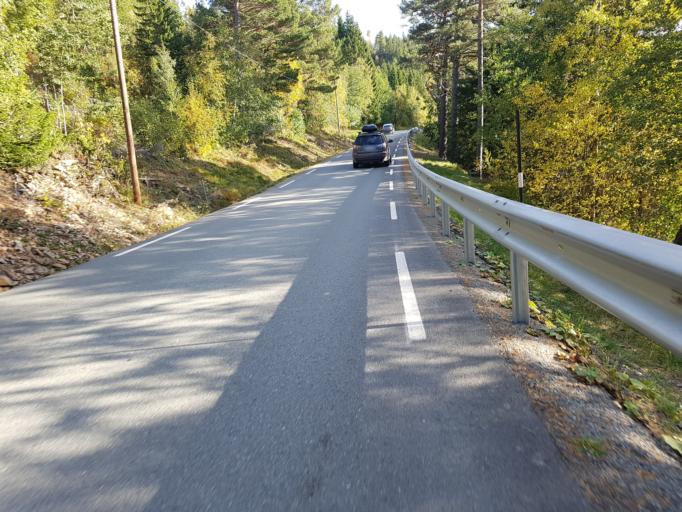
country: NO
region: Sor-Trondelag
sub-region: Malvik
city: Malvik
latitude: 63.3679
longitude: 10.6191
